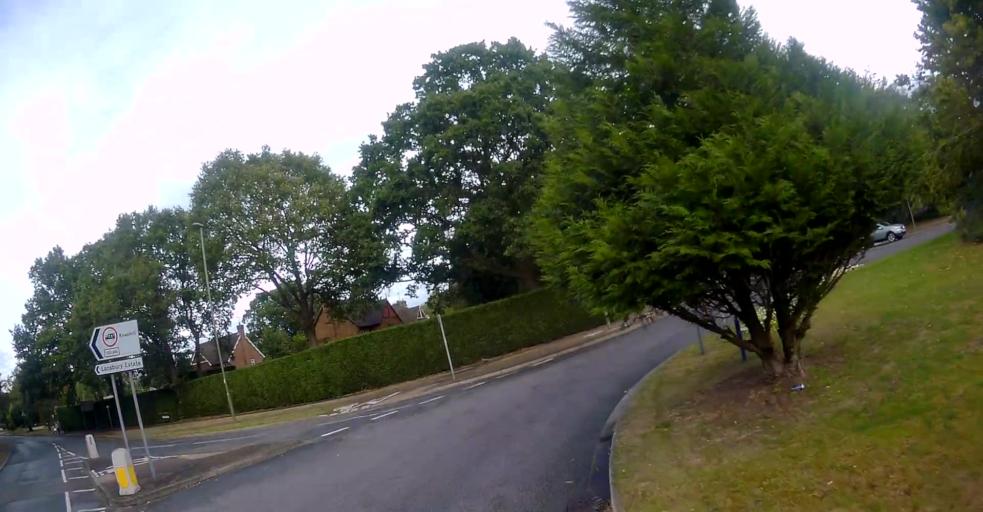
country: GB
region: England
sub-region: Surrey
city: Knaphill
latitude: 51.3117
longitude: -0.6141
